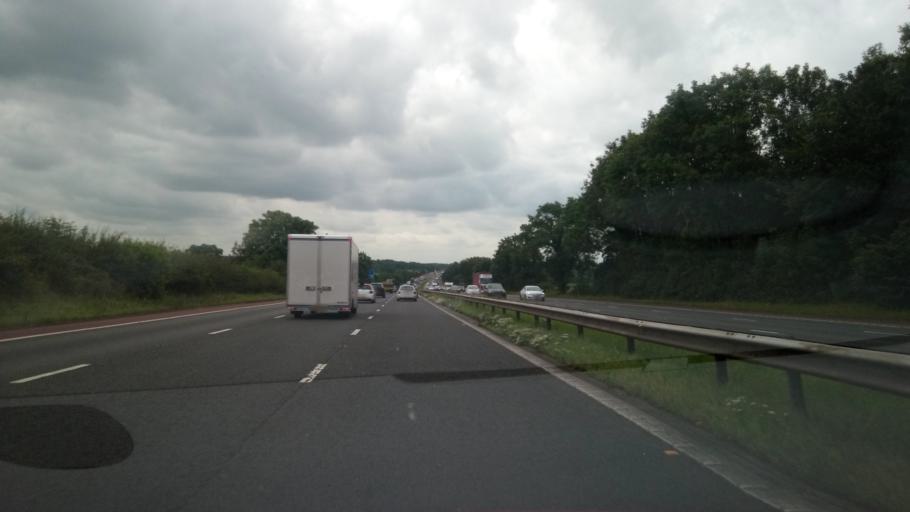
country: GB
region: England
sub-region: Lancashire
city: Galgate
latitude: 54.0078
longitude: -2.7808
